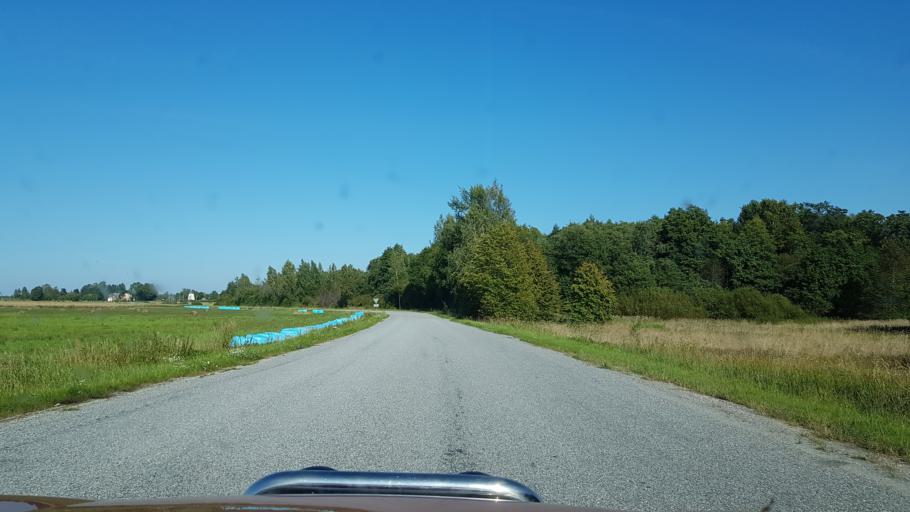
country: EE
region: Polvamaa
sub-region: Raepina vald
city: Rapina
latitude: 58.2178
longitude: 27.4384
